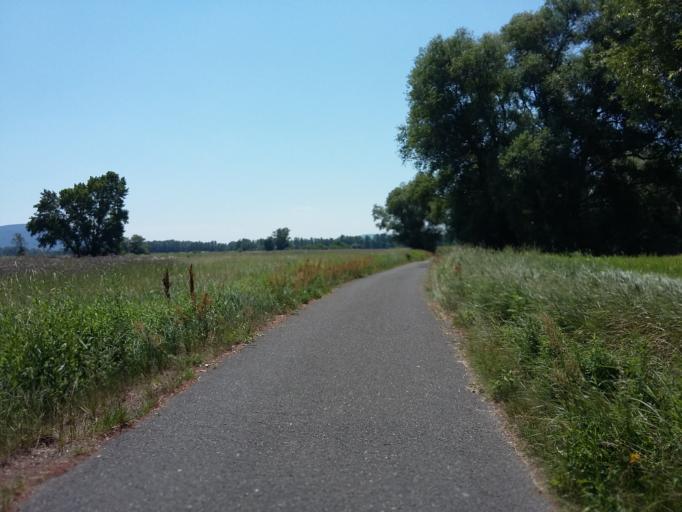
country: AT
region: Lower Austria
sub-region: Politischer Bezirk Ganserndorf
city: Marchegg
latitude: 48.2526
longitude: 16.9532
